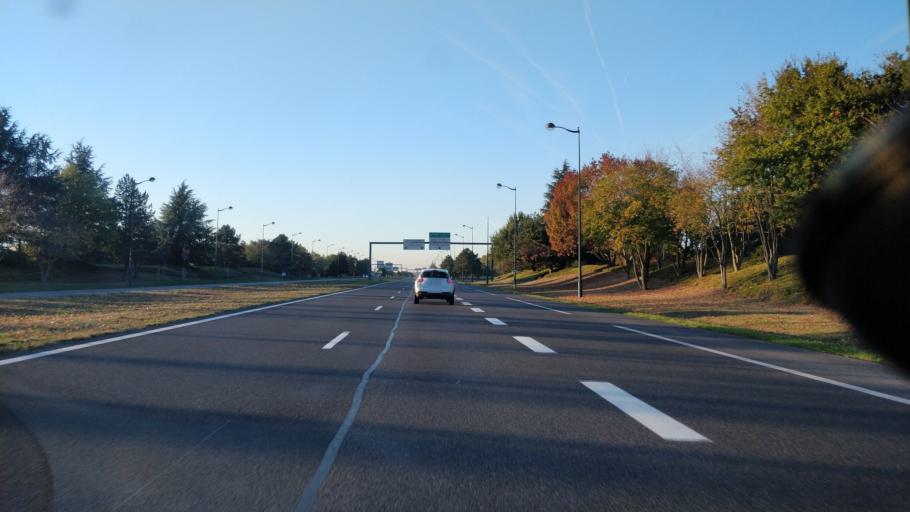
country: FR
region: Ile-de-France
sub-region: Departement de Seine-et-Marne
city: Magny-le-Hongre
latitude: 48.8511
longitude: 2.8050
